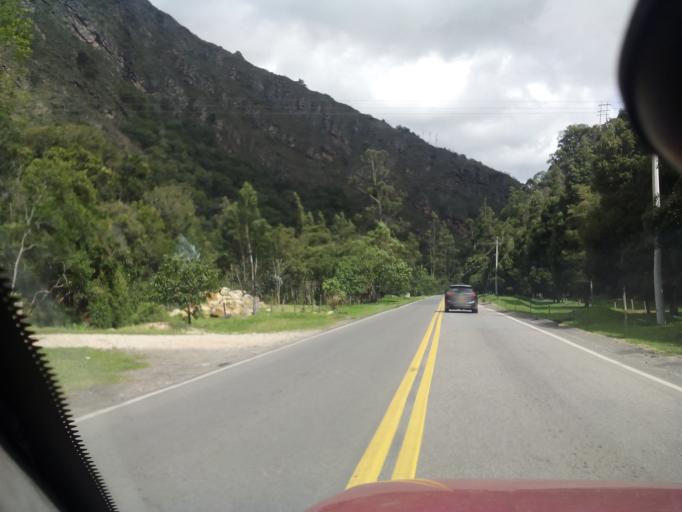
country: CO
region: Boyaca
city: Arcabuco
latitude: 5.7464
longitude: -73.4293
